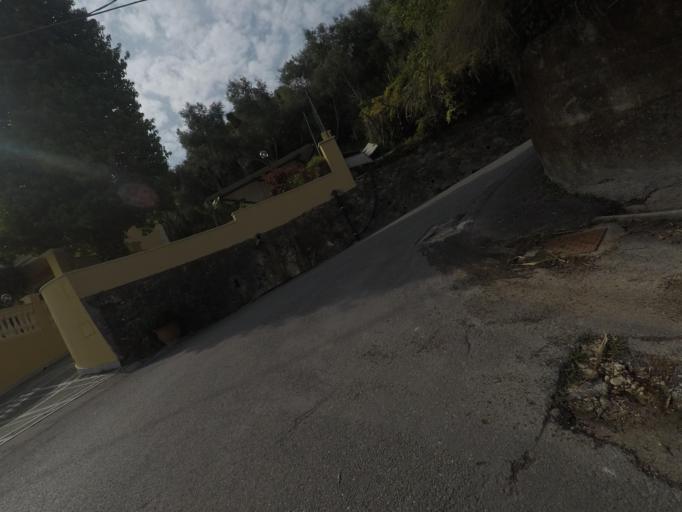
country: IT
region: Tuscany
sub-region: Provincia di Massa-Carrara
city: Massa
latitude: 44.0487
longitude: 10.0990
